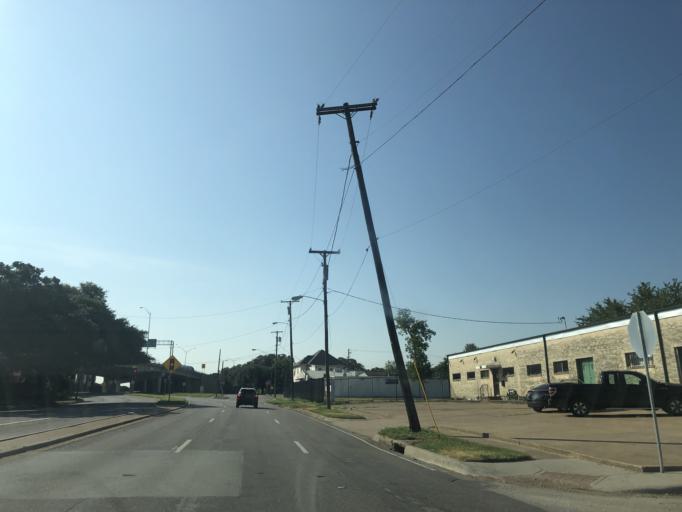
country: US
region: Texas
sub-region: Dallas County
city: Dallas
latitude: 32.7680
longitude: -96.7787
